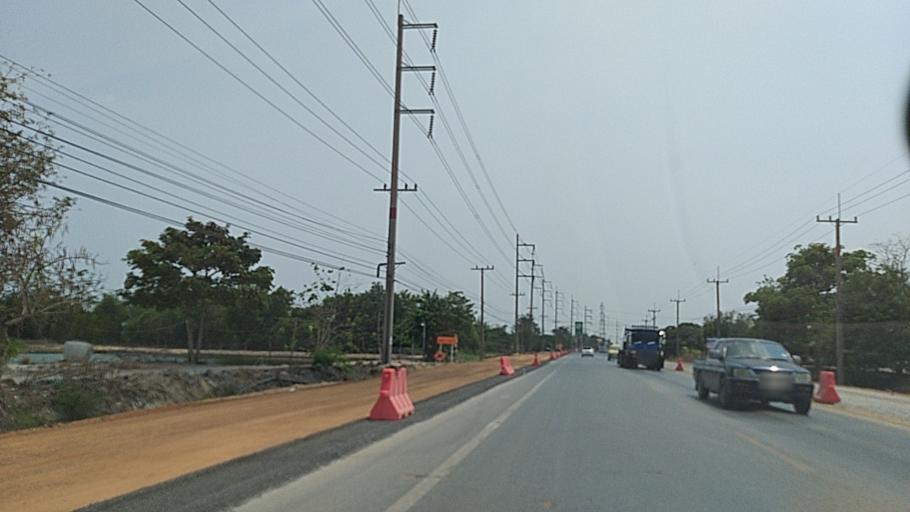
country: TH
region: Chachoengsao
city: Ban Pho
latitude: 13.5871
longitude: 101.1227
